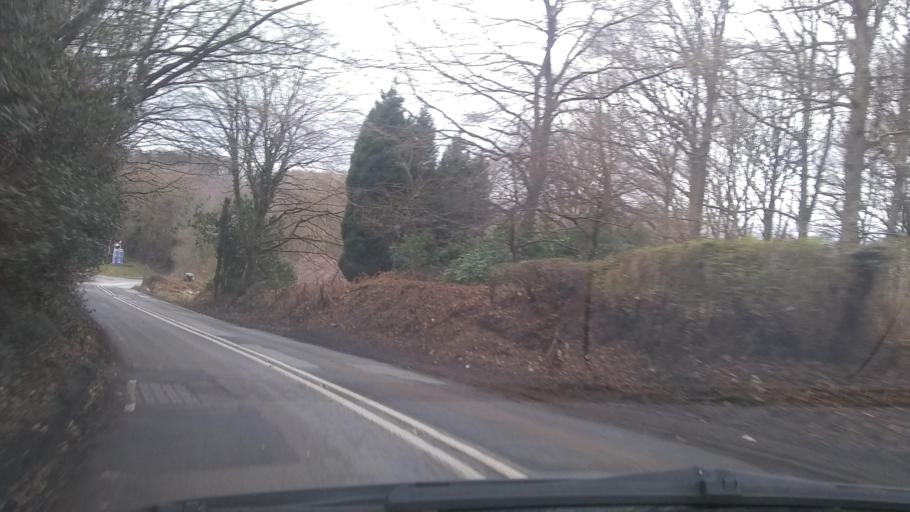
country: GB
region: England
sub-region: Shropshire
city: Cleobury Mortimer
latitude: 52.3772
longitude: -2.4359
